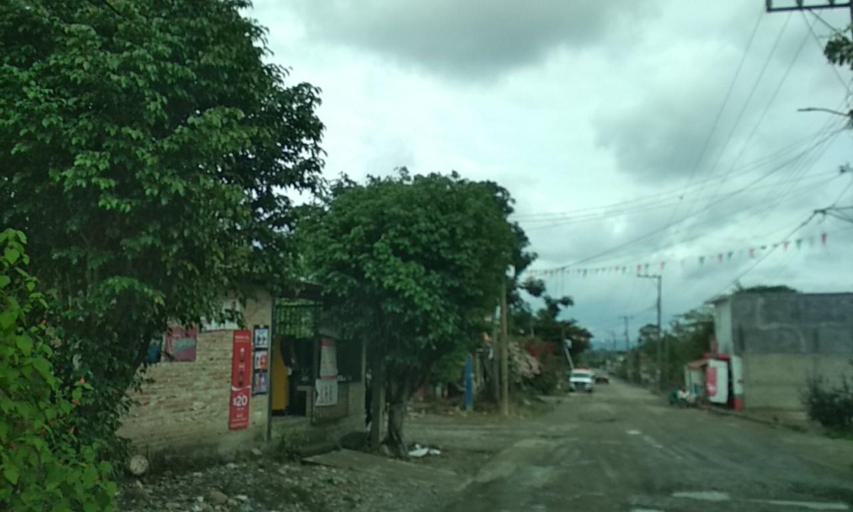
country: MX
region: Veracruz
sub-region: Papantla
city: El Chote
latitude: 20.3581
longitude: -97.3398
